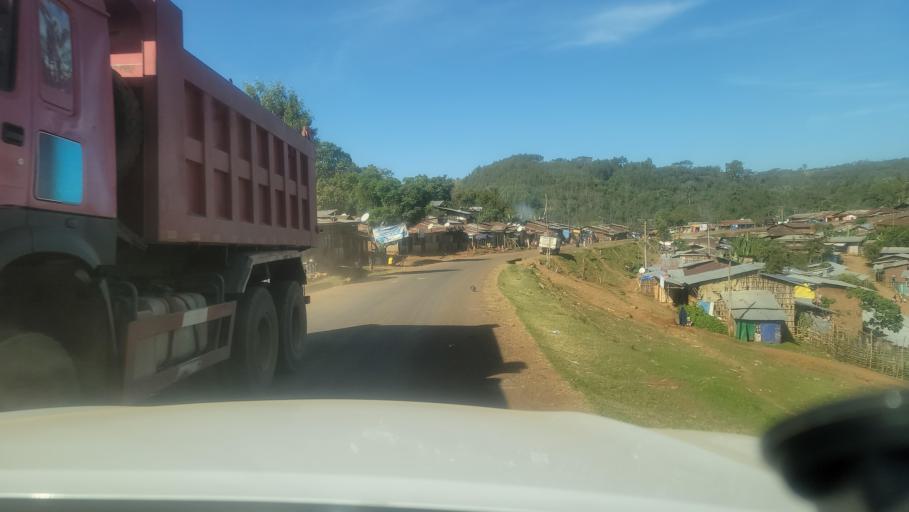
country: ET
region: Oromiya
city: Agaro
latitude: 7.7951
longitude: 36.4796
